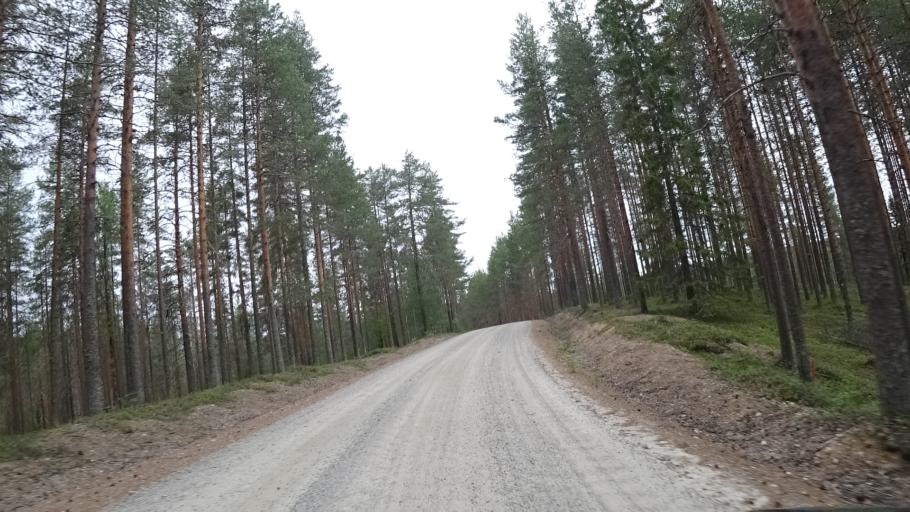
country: FI
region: North Karelia
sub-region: Pielisen Karjala
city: Lieksa
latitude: 63.2099
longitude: 30.4175
